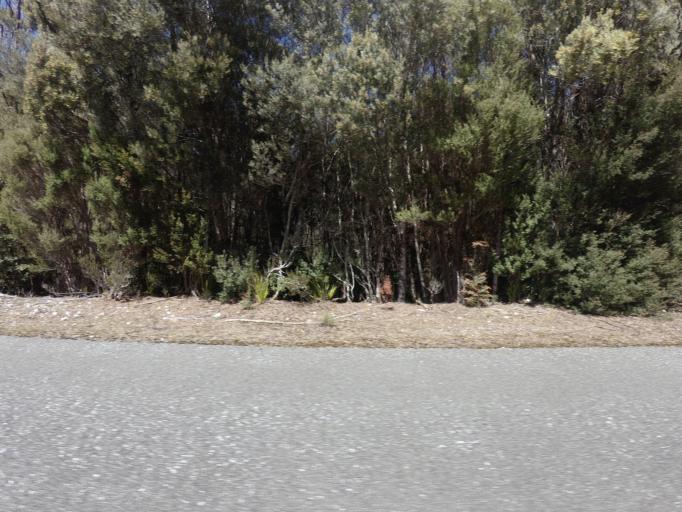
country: AU
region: Tasmania
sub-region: West Coast
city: Queenstown
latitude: -42.7681
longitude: 146.0174
